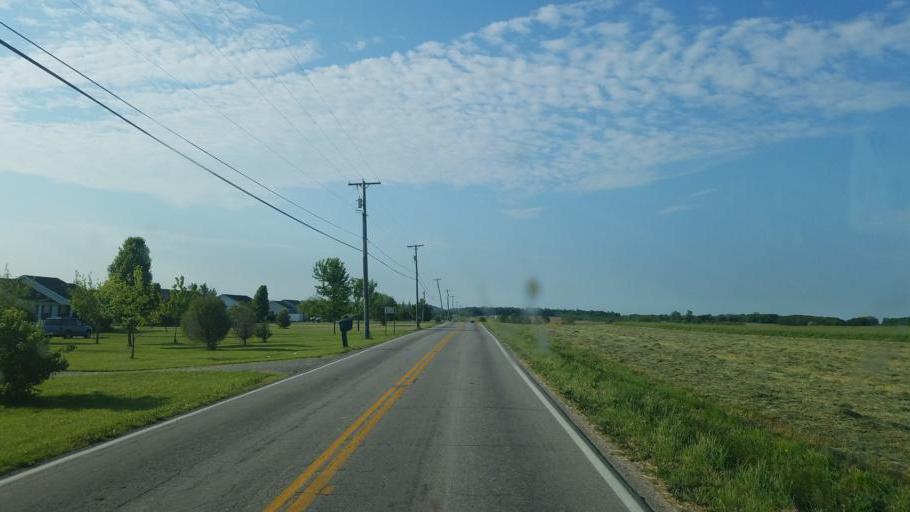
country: US
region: Ohio
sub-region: Highland County
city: Greenfield
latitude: 39.2595
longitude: -83.4427
